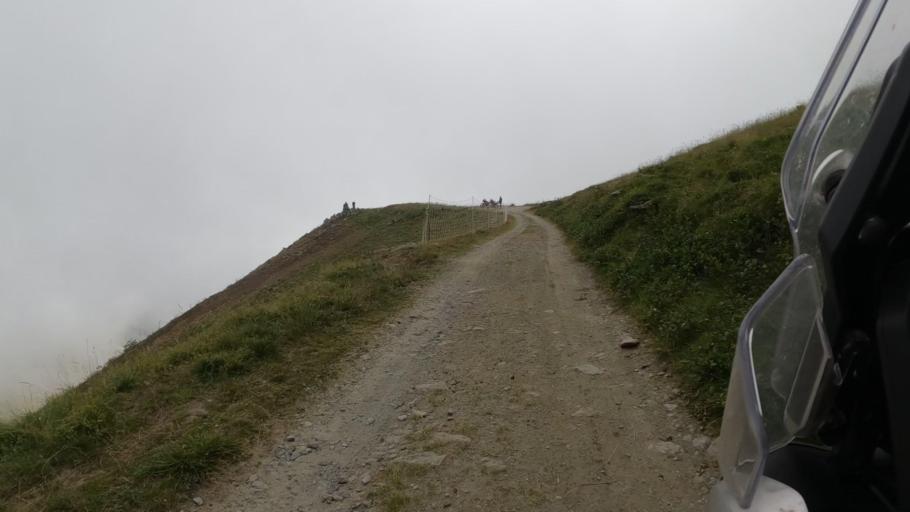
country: IT
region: Piedmont
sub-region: Provincia di Torino
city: Lemie
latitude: 45.1800
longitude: 7.2833
